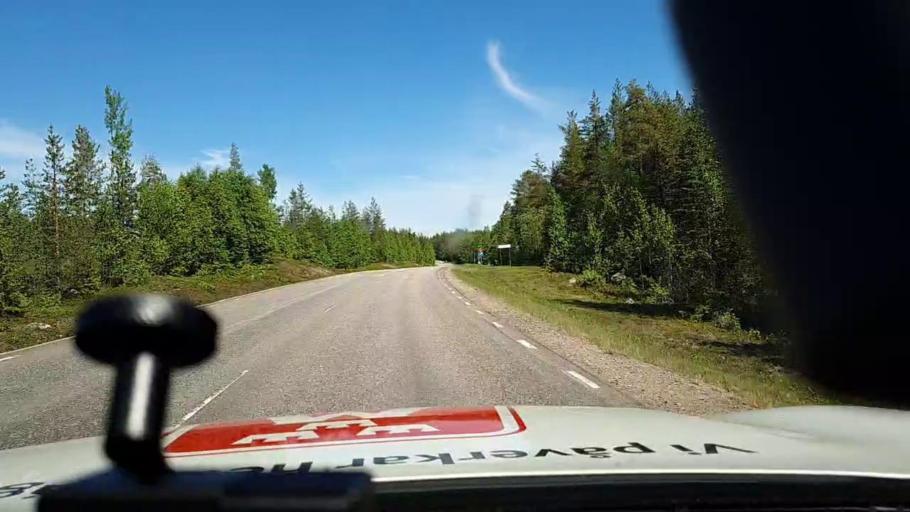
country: SE
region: Norrbotten
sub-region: Overkalix Kommun
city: OEverkalix
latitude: 66.1662
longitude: 22.8030
